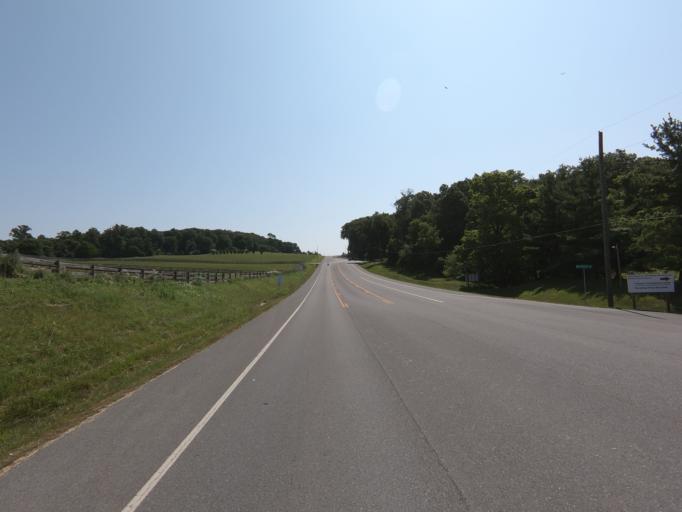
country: US
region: Maryland
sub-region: Frederick County
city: Bartonsville
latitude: 39.3753
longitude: -77.3513
